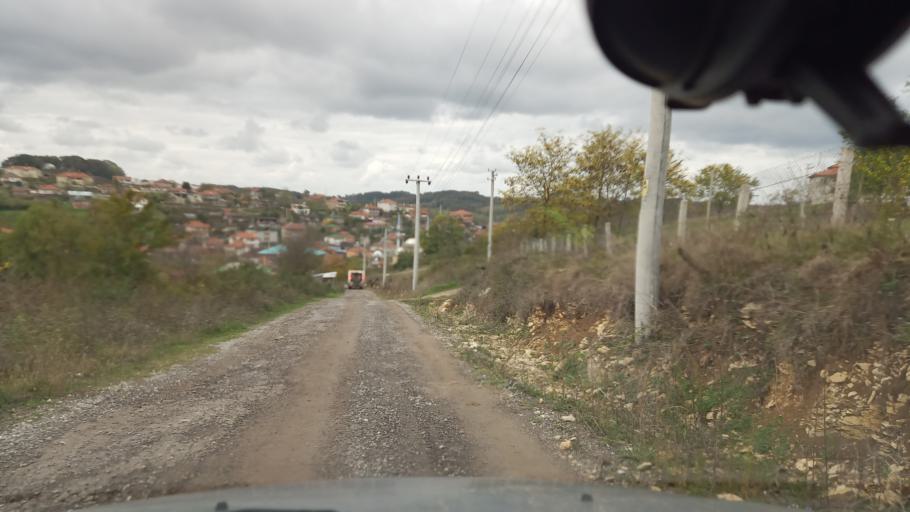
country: TR
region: Sakarya
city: Karasu
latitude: 41.0910
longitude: 30.5855
